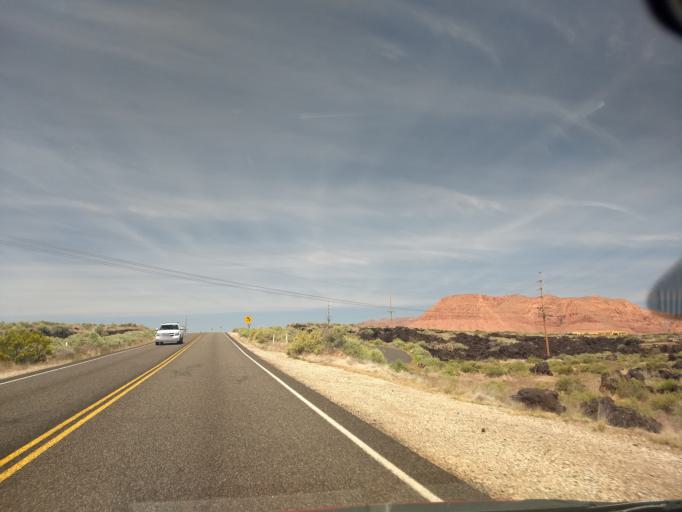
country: US
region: Utah
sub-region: Washington County
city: Santa Clara
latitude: 37.1430
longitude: -113.6450
